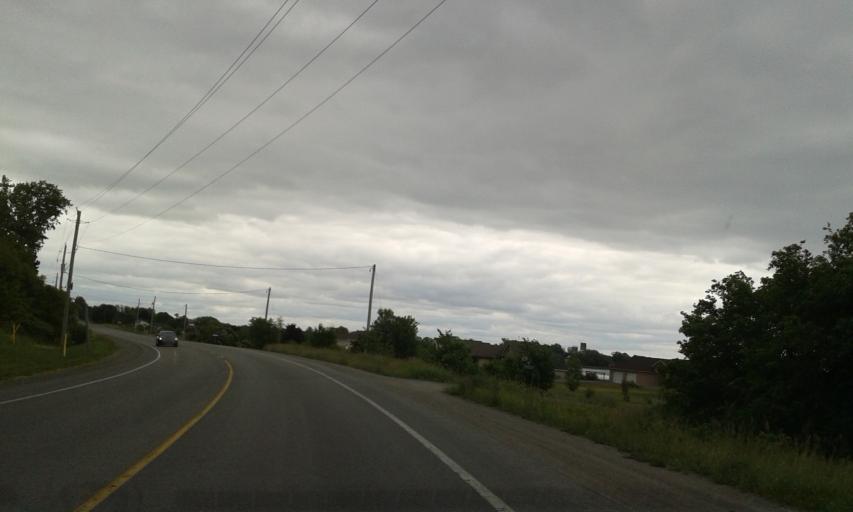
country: CA
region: Ontario
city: Quinte West
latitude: 43.9618
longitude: -77.4963
